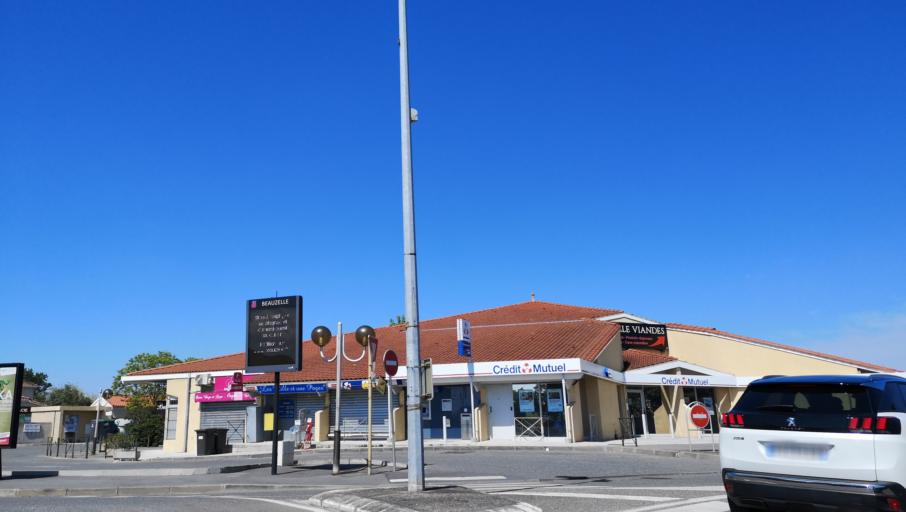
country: FR
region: Midi-Pyrenees
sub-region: Departement de la Haute-Garonne
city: Beauzelle
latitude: 43.6699
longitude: 1.3682
